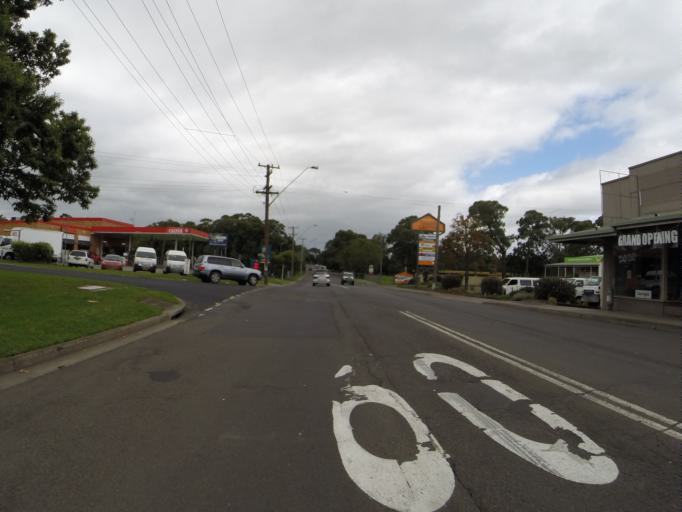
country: AU
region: New South Wales
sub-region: Shoalhaven Shire
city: Bomaderry
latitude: -34.8583
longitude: 150.6049
